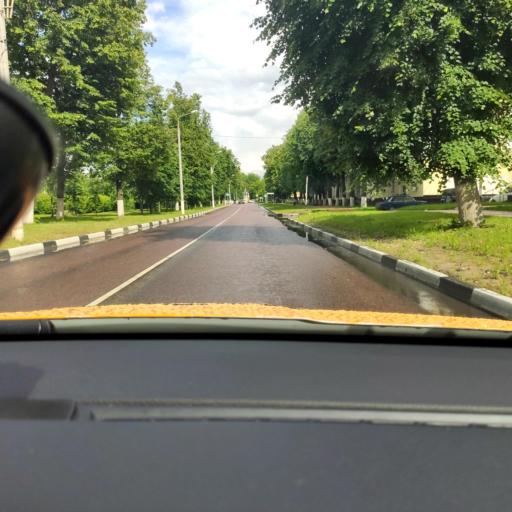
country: RU
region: Moskovskaya
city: Stupino
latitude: 54.8900
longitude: 38.0742
